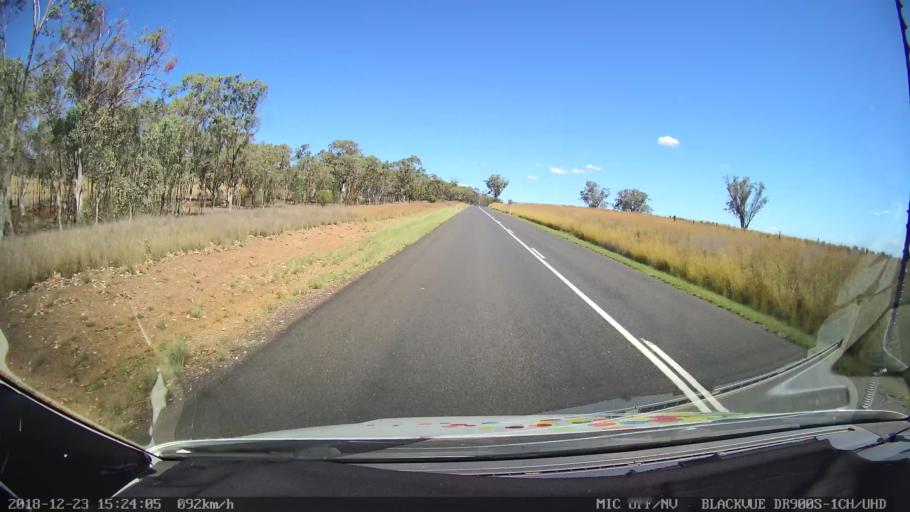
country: AU
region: New South Wales
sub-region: Tamworth Municipality
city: Manilla
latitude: -30.8876
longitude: 150.8203
